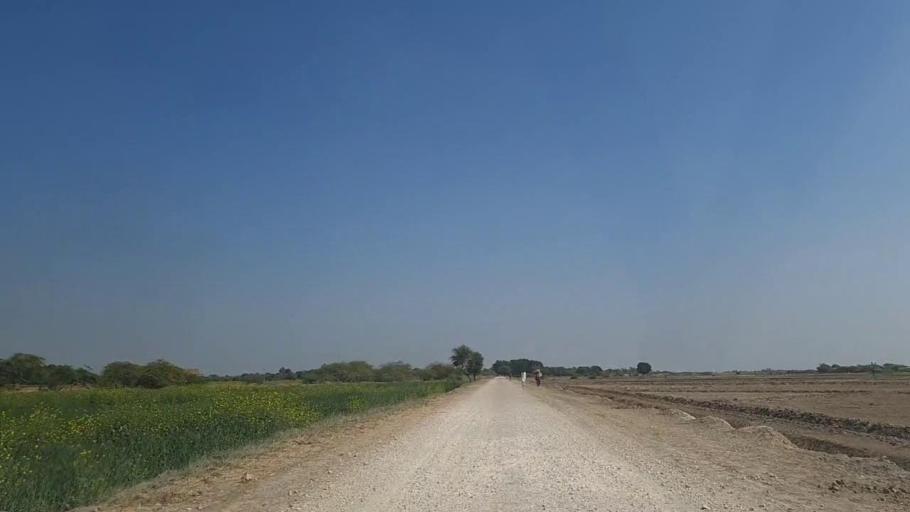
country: PK
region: Sindh
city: Digri
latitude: 25.1616
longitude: 69.1863
